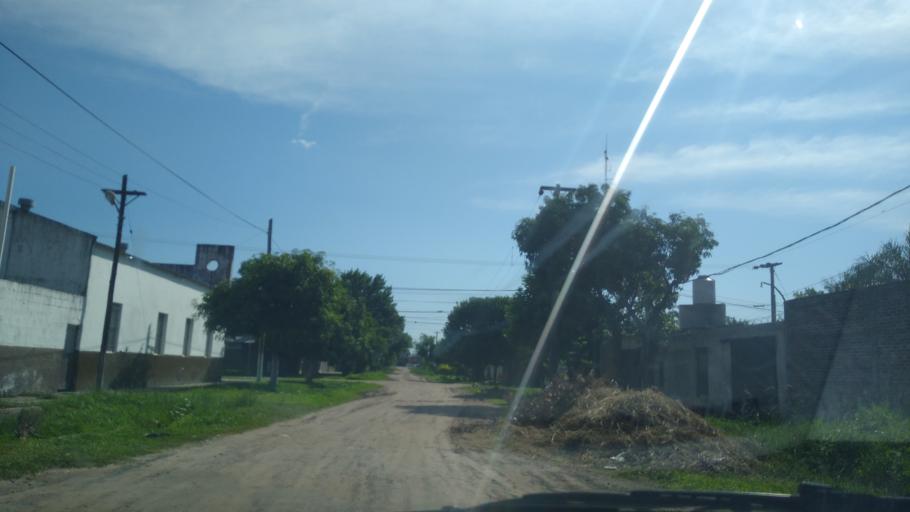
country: AR
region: Chaco
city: Barranqueras
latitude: -27.4884
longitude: -58.9545
